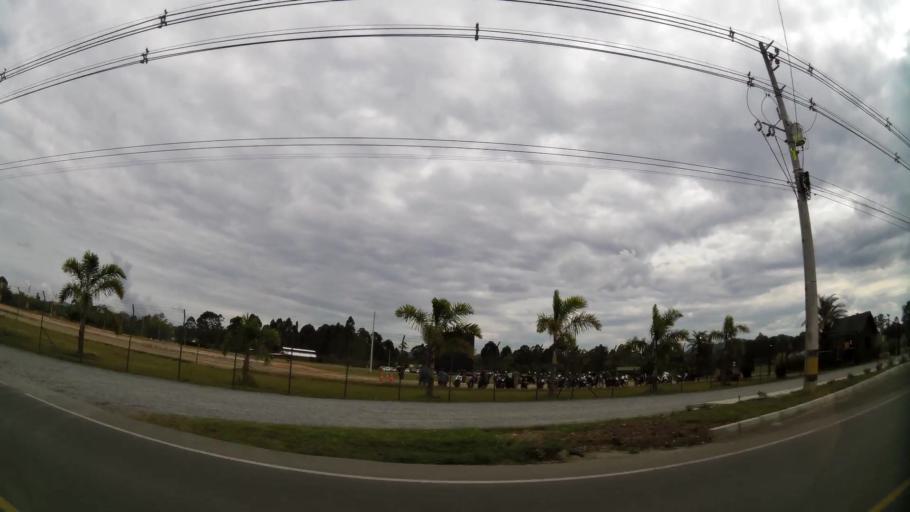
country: CO
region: Antioquia
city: Rionegro
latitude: 6.1463
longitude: -75.4266
